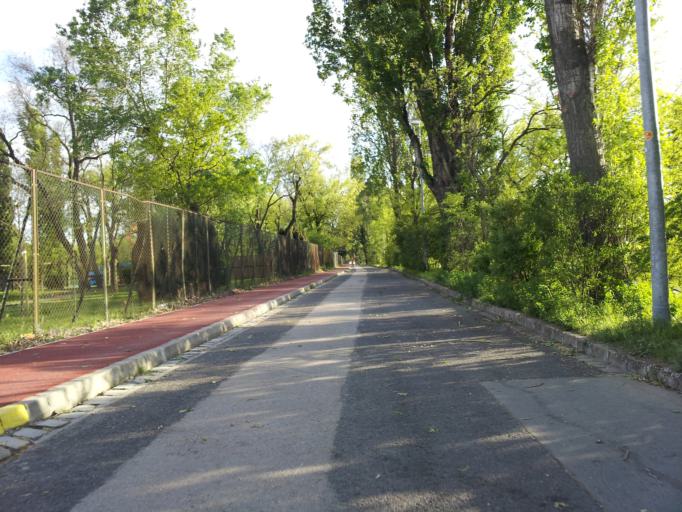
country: HU
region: Budapest
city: Budapest III. keruelet
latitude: 47.5285
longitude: 19.0454
